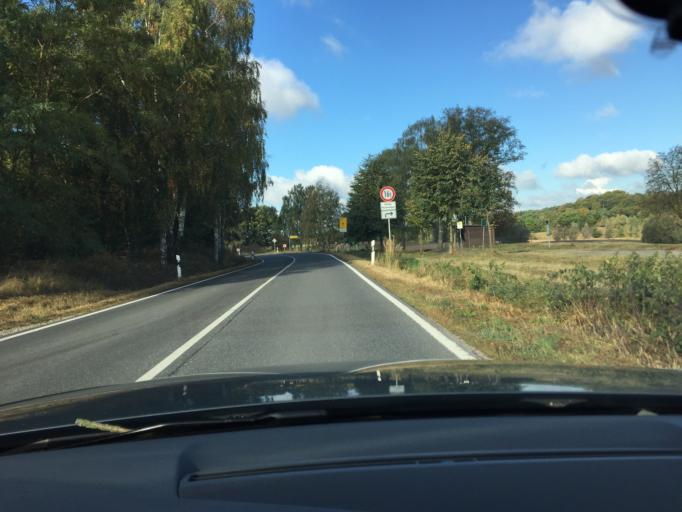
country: DE
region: Mecklenburg-Vorpommern
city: Krakow am See
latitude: 53.6855
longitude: 12.3207
